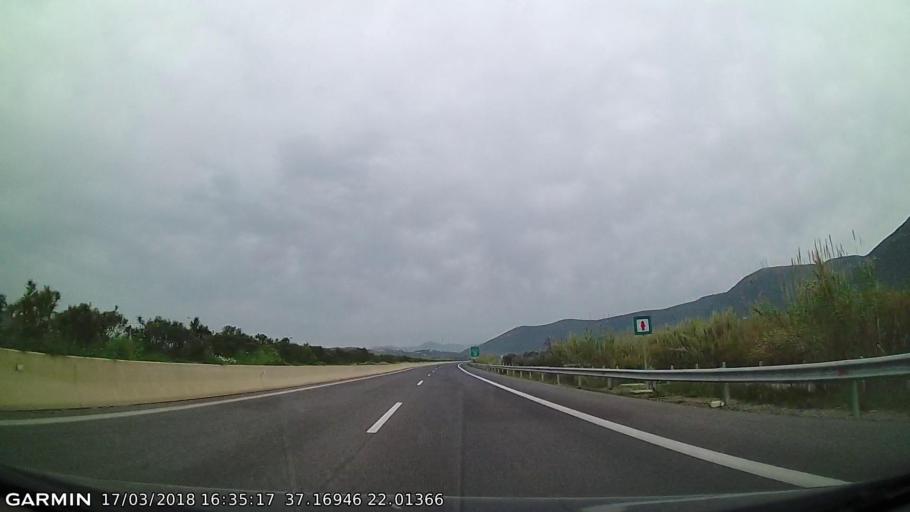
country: GR
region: Peloponnese
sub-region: Nomos Messinias
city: Arfara
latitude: 37.1699
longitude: 22.0135
